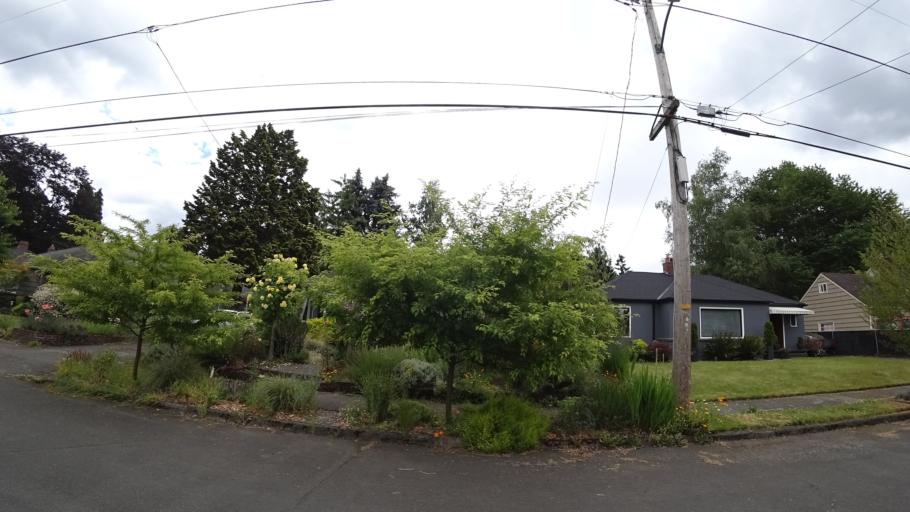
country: US
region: Oregon
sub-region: Multnomah County
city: Portland
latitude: 45.5614
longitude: -122.5984
